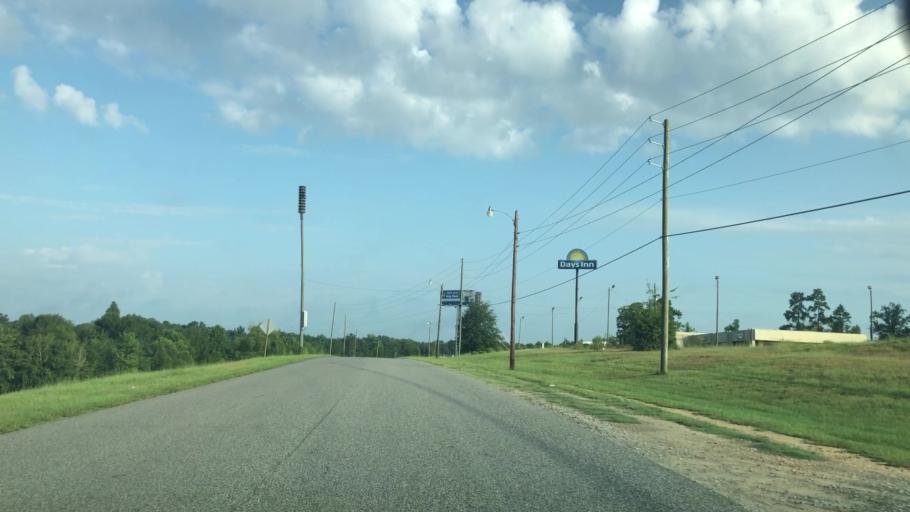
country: US
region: Alabama
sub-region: Chilton County
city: Clanton
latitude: 32.8025
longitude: -86.5774
